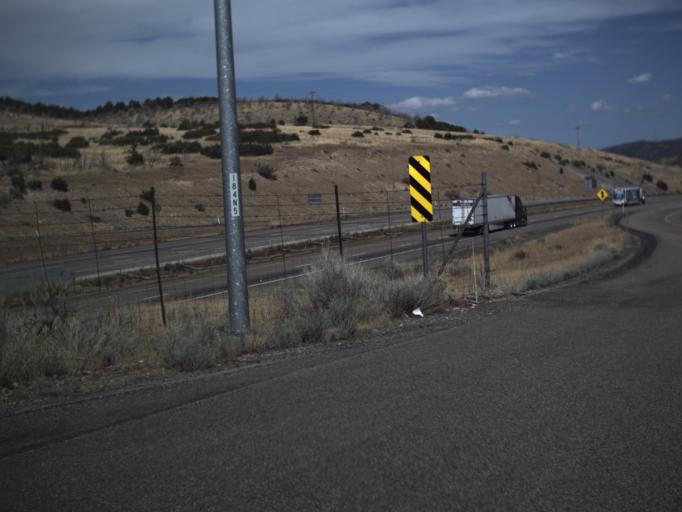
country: US
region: Utah
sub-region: Millard County
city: Fillmore
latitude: 39.2023
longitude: -112.1731
